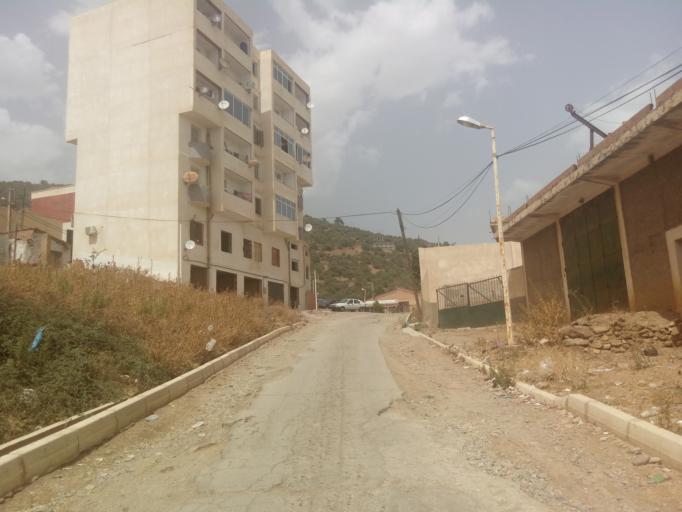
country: DZ
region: Tizi Ouzou
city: Chemini
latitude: 36.6049
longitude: 4.6389
